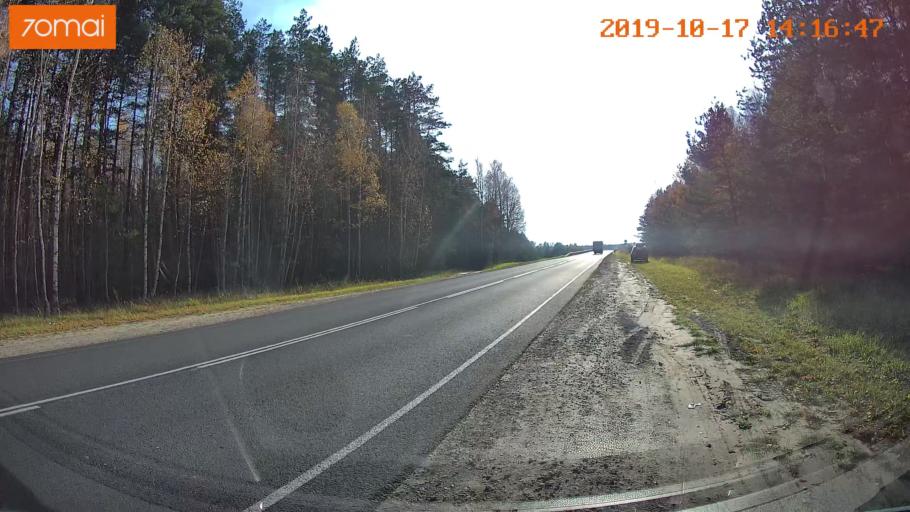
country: RU
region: Rjazan
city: Spas-Klepiki
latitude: 55.0781
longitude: 40.0494
